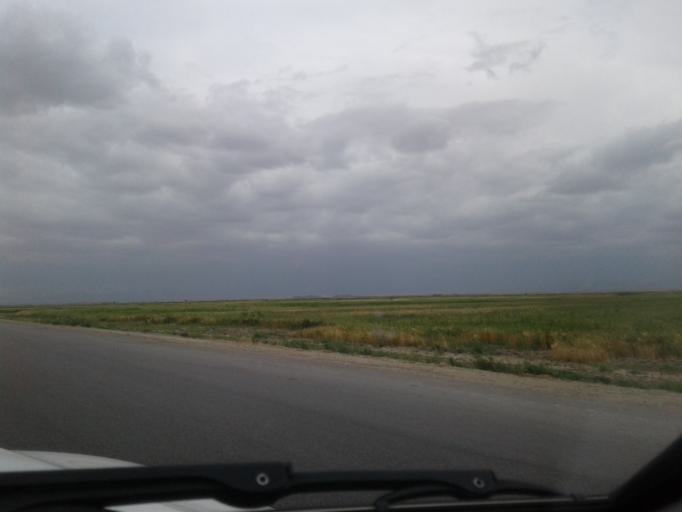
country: TM
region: Ahal
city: Kaka
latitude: 37.4526
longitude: 59.5153
